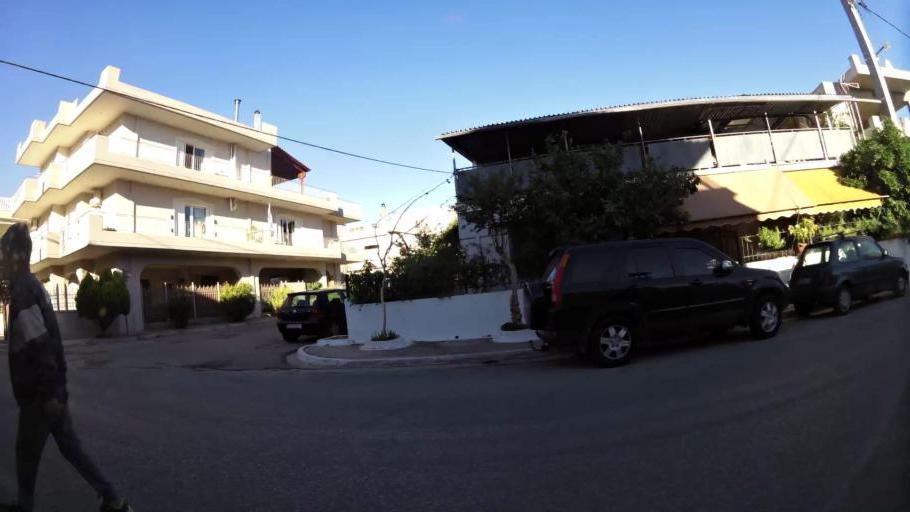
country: GR
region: Attica
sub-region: Nomarchia Anatolikis Attikis
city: Acharnes
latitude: 38.0871
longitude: 23.7232
